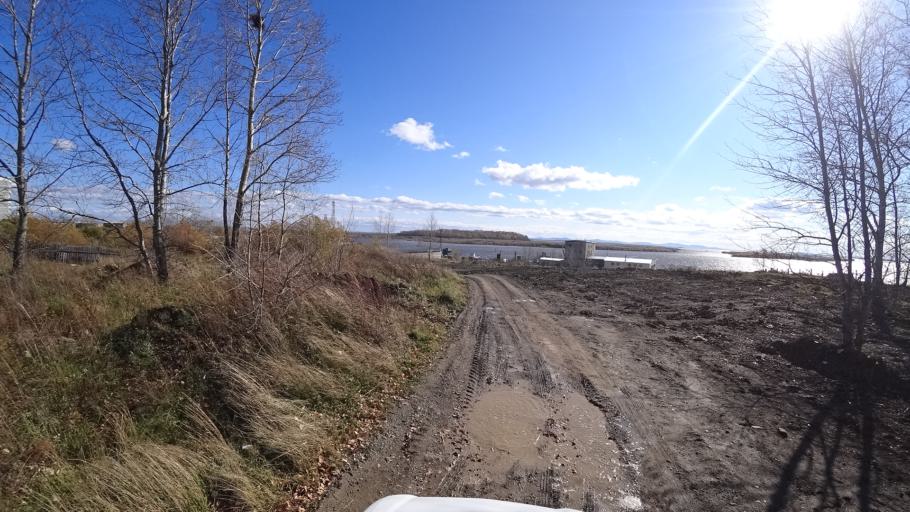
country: RU
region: Khabarovsk Krai
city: Amursk
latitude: 50.2151
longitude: 136.8891
